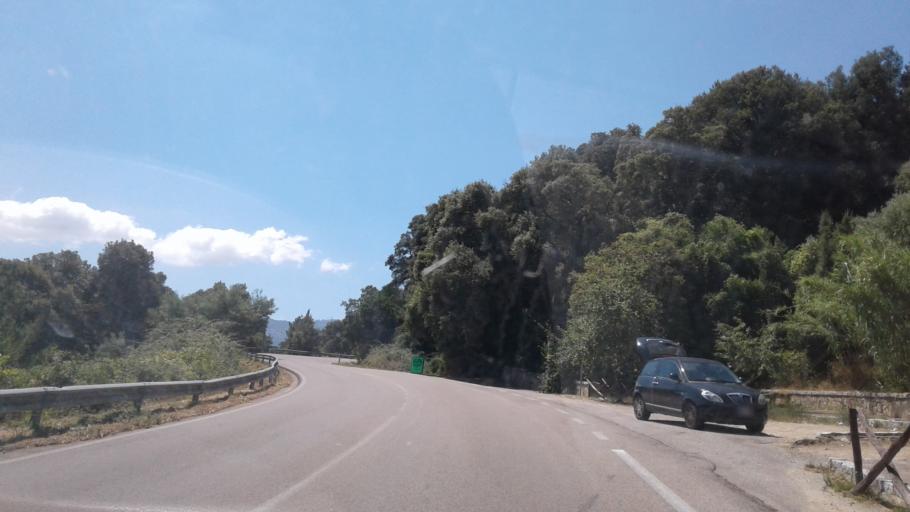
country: IT
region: Sardinia
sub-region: Provincia di Olbia-Tempio
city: Luras
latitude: 40.9317
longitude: 9.1817
